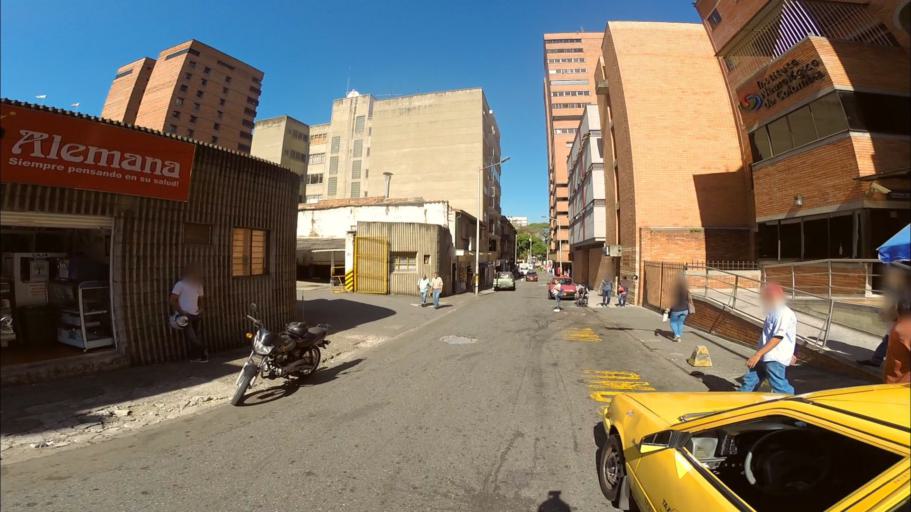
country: CO
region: Antioquia
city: Medellin
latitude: 6.2522
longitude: -75.5635
